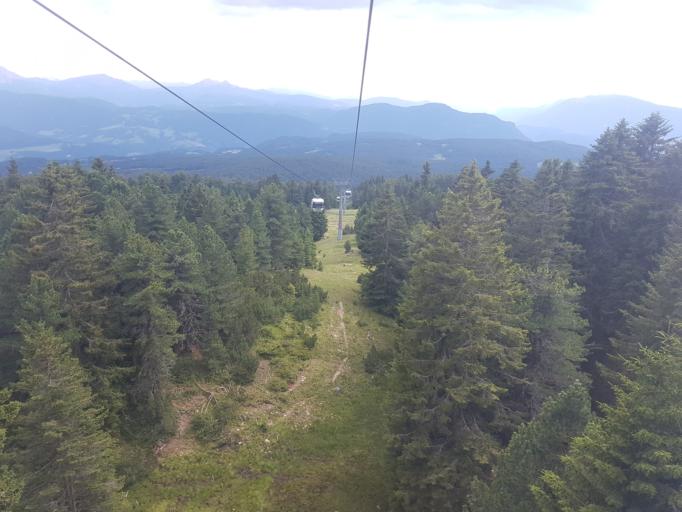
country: IT
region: Trentino-Alto Adige
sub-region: Bolzano
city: Renon - Ritten
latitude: 46.5861
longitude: 11.4492
